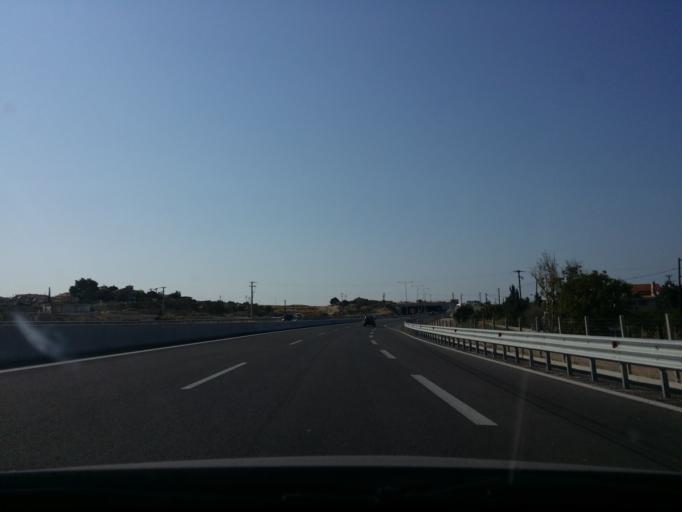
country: GR
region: Peloponnese
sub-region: Nomos Korinthias
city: Xylokastro
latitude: 38.0593
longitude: 22.6580
